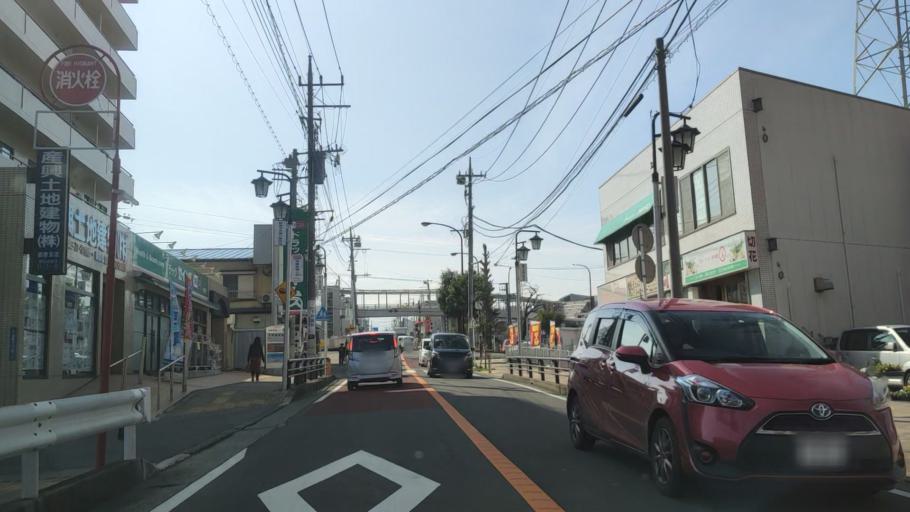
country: JP
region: Kanagawa
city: Isehara
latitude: 35.3820
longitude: 139.2787
